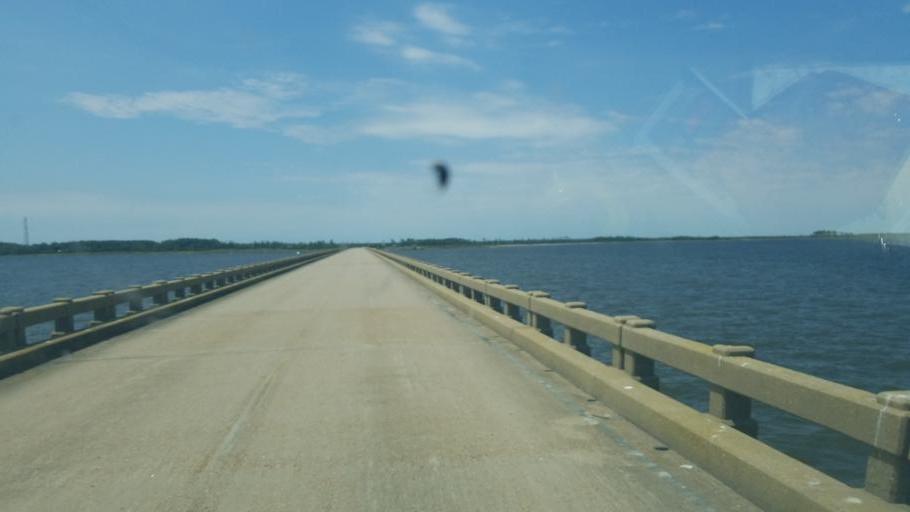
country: US
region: North Carolina
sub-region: Dare County
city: Manteo
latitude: 35.9149
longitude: -75.7586
